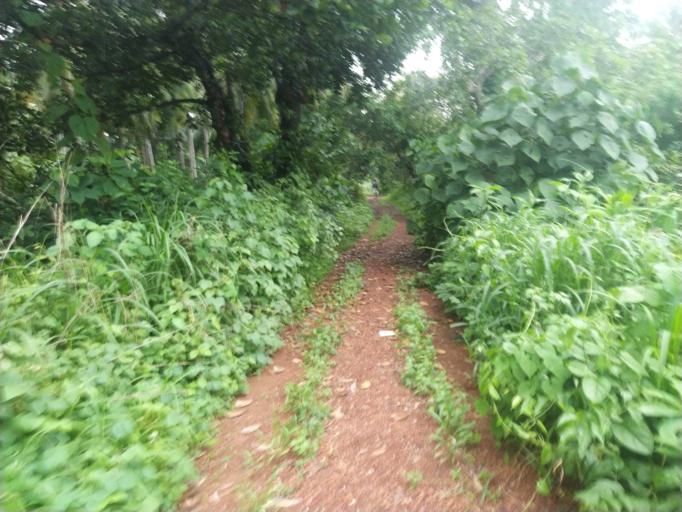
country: IN
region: Kerala
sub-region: Kasaragod District
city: Kannangad
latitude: 12.4037
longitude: 75.0586
